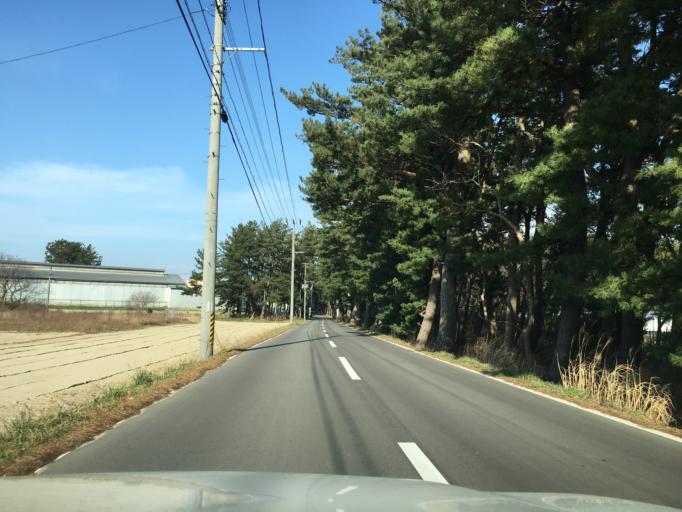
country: JP
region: Yamagata
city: Tsuruoka
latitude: 38.8051
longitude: 139.7756
